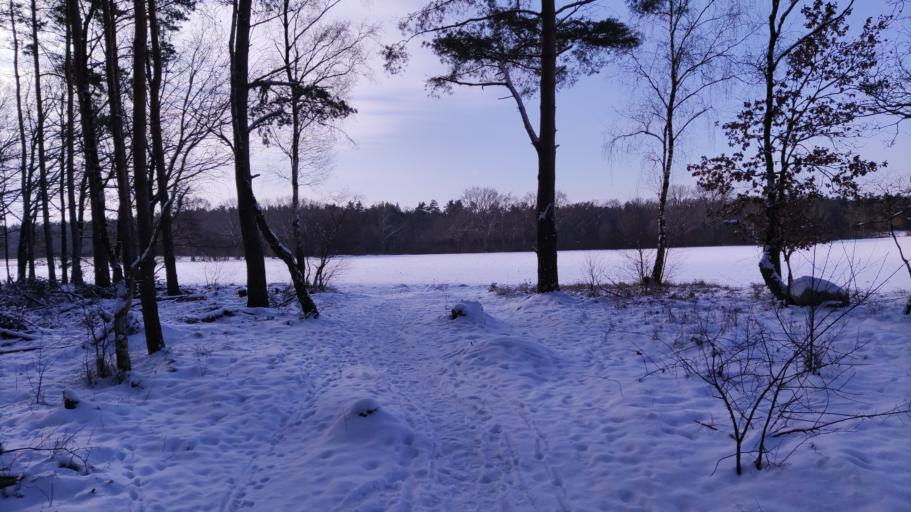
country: DE
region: Lower Saxony
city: Deutsch Evern
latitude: 53.2293
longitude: 10.4392
